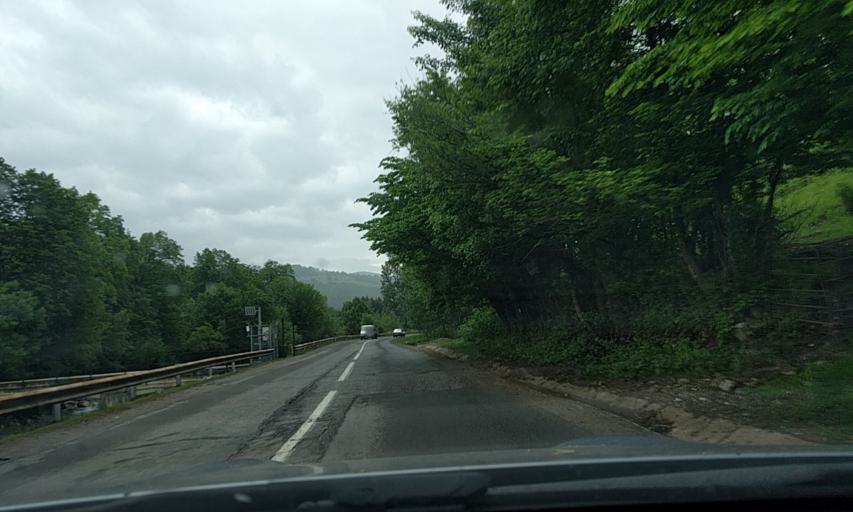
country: RO
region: Dambovita
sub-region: Comuna Moroeni
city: Moroeni
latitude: 45.2304
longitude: 25.4380
